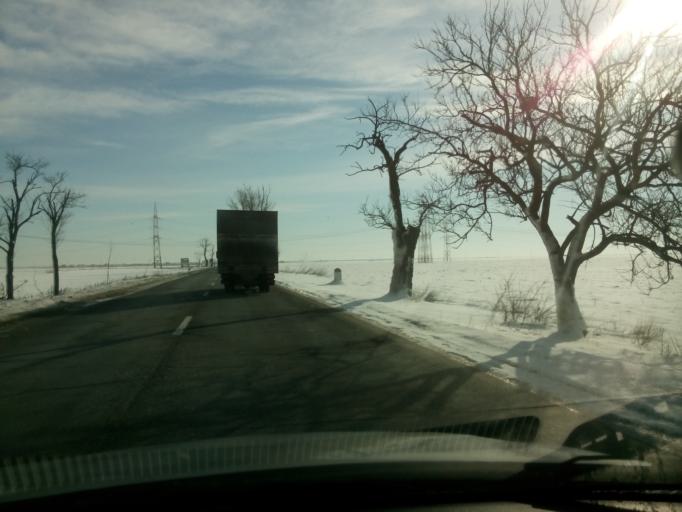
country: RO
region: Ilfov
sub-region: Comuna Glina
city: Glina
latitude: 44.3516
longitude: 26.2149
